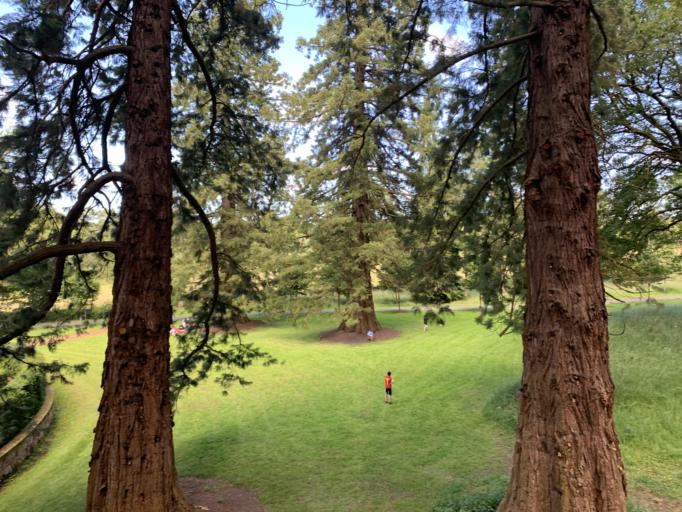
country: GB
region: Scotland
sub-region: East Ayrshire
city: Auchinleck
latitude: 55.4571
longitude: -4.3119
